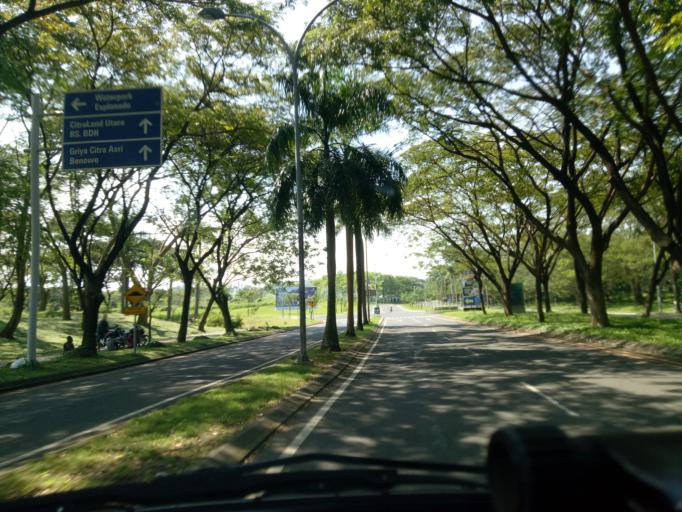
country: ID
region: East Java
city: Driyorejo
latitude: -7.2877
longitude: 112.6351
